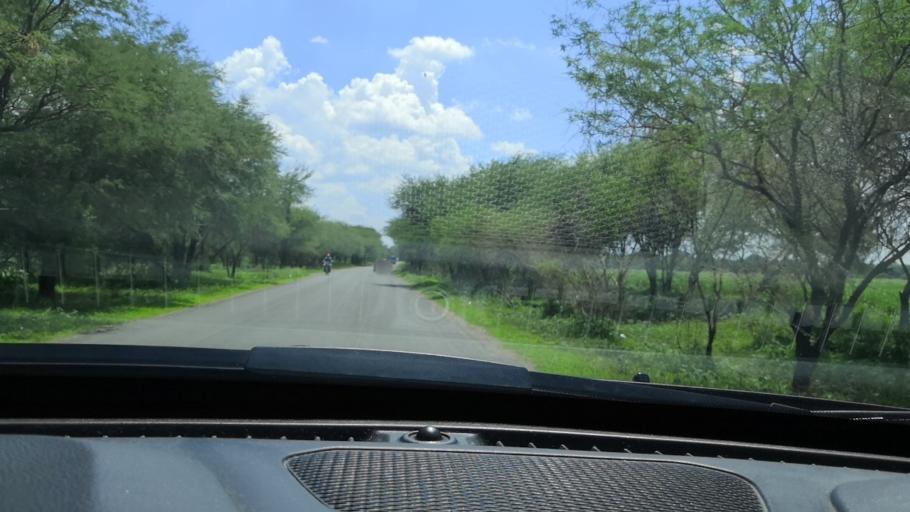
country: MX
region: Guanajuato
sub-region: Leon
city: Plan Guanajuato (La Sandia)
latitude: 20.9389
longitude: -101.6338
